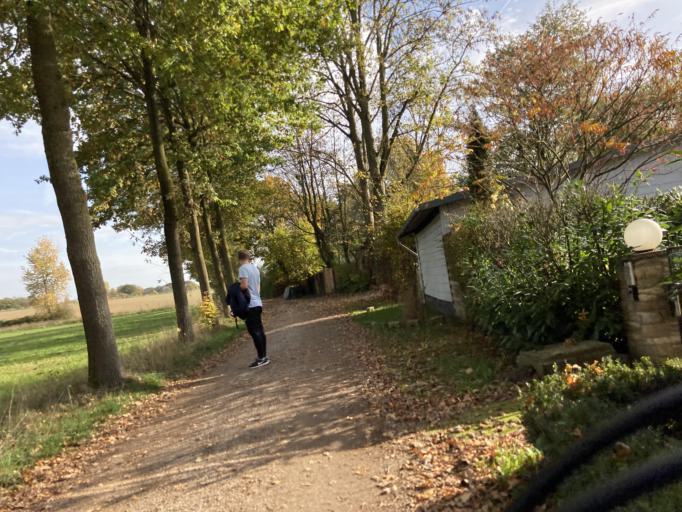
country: DE
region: North Rhine-Westphalia
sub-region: Regierungsbezirk Munster
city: Muenster
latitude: 51.9735
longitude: 7.7008
